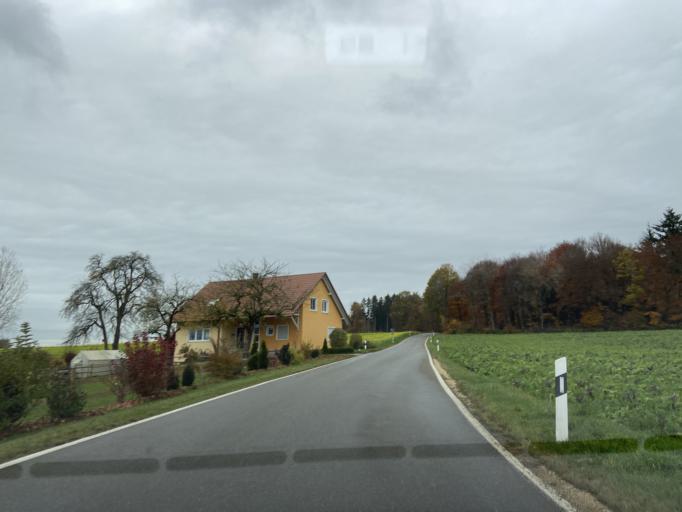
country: DE
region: Baden-Wuerttemberg
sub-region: Tuebingen Region
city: Wald
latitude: 47.9644
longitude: 9.1928
